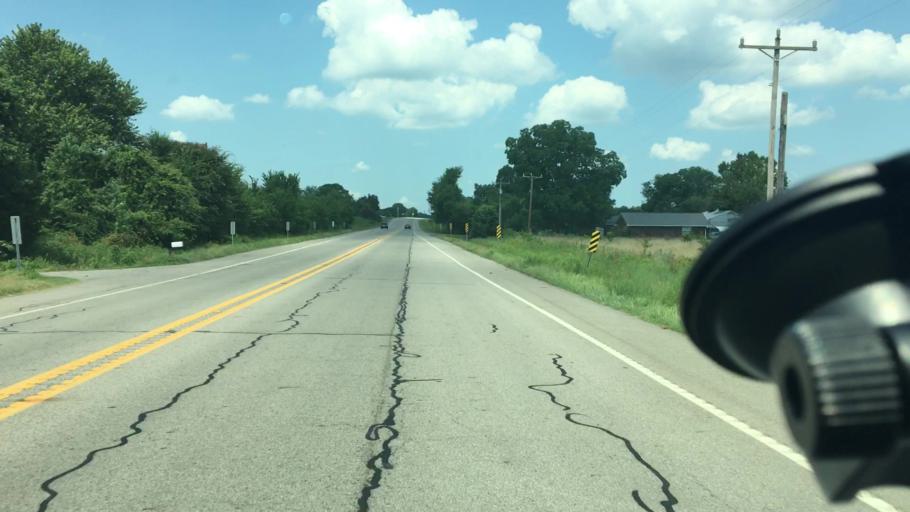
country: US
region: Arkansas
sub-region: Logan County
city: Paris
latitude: 35.2987
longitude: -93.8214
